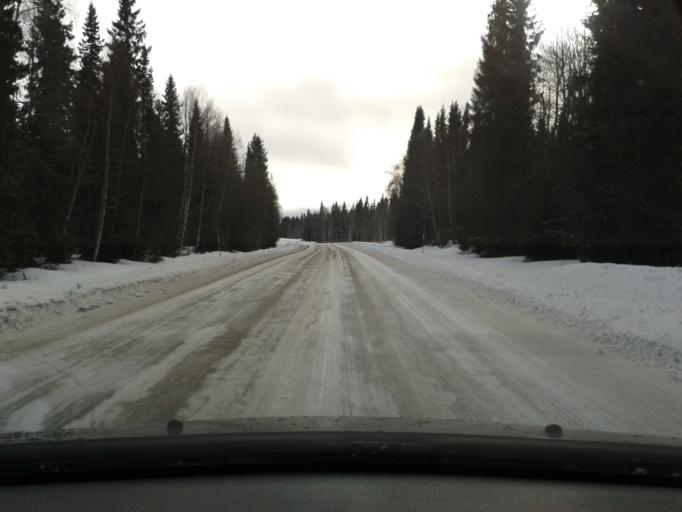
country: SE
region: Vaesterbotten
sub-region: Vilhelmina Kommun
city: Sjoberg
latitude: 64.7230
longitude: 16.2301
